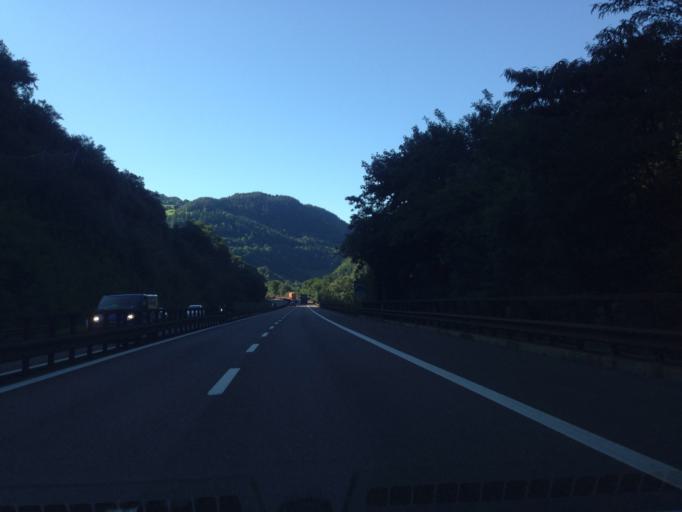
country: IT
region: Trentino-Alto Adige
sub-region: Bolzano
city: Ponte Gardena
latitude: 46.5808
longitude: 11.5238
